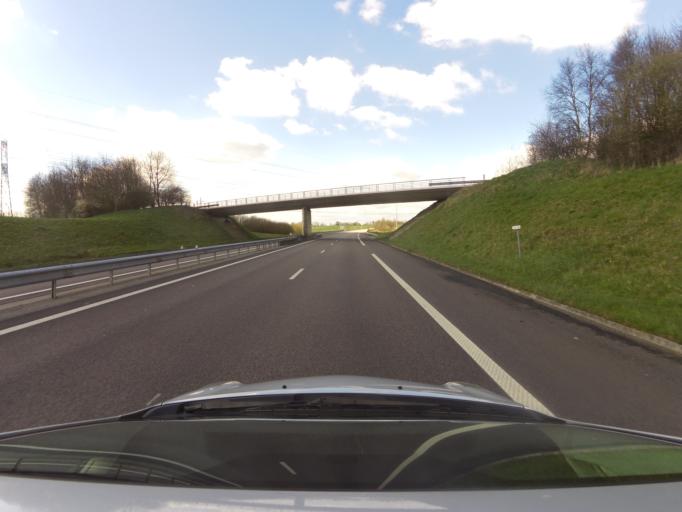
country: FR
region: Haute-Normandie
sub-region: Departement de la Seine-Maritime
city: Totes
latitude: 49.6374
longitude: 1.0375
